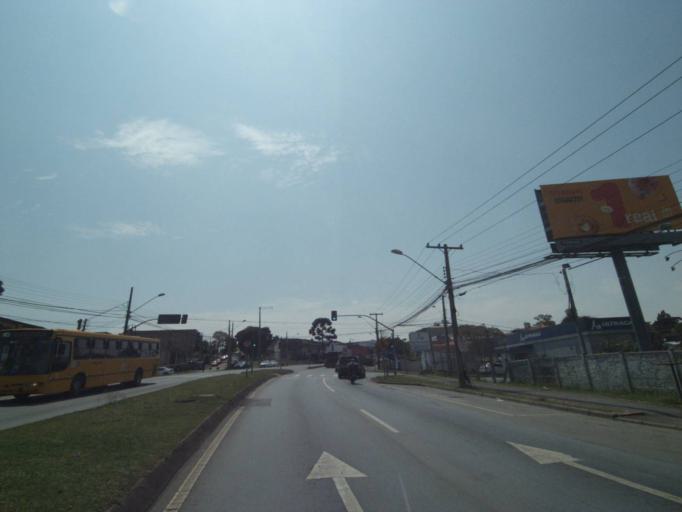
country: BR
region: Parana
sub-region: Curitiba
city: Curitiba
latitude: -25.4797
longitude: -49.3146
